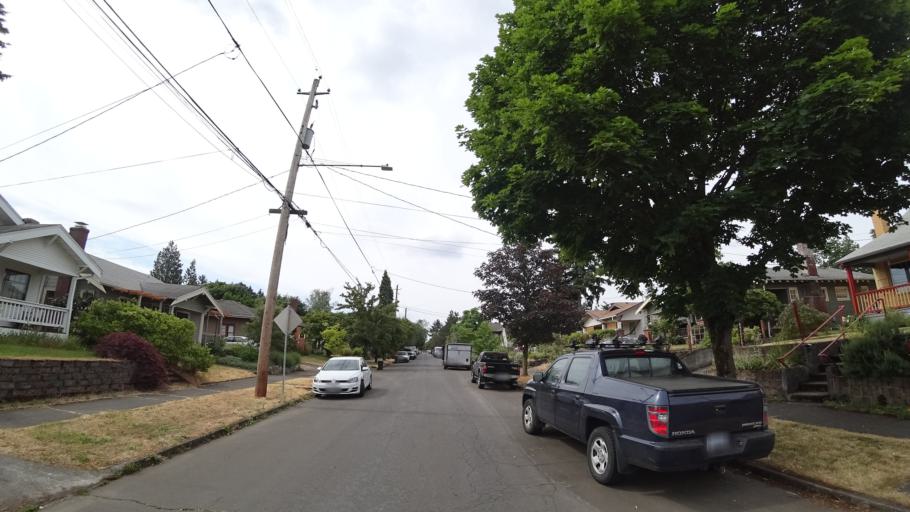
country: US
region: Oregon
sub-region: Multnomah County
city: Portland
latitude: 45.5714
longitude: -122.6759
